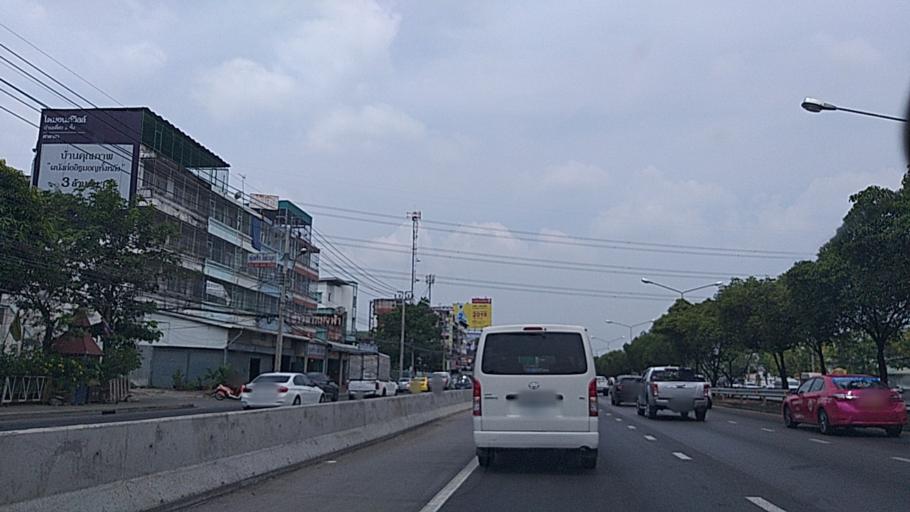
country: TH
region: Bangkok
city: Thawi Watthana
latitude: 13.7871
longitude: 100.3674
